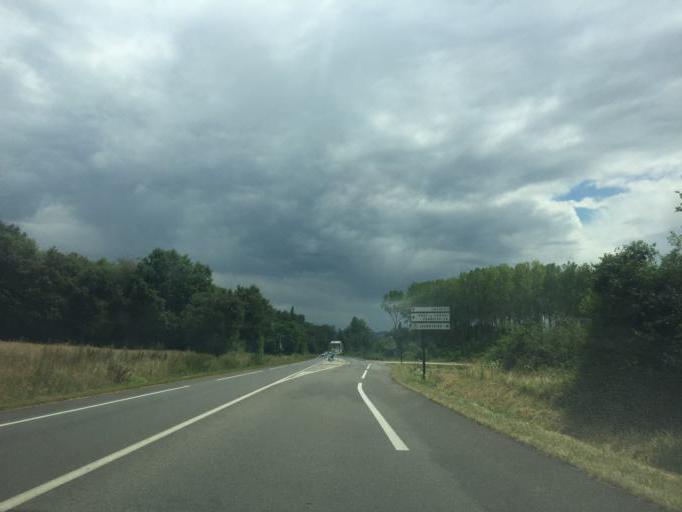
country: FR
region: Rhone-Alpes
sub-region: Departement de l'Isere
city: Charvieu-Chavagneux
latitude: 45.7561
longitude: 5.1332
